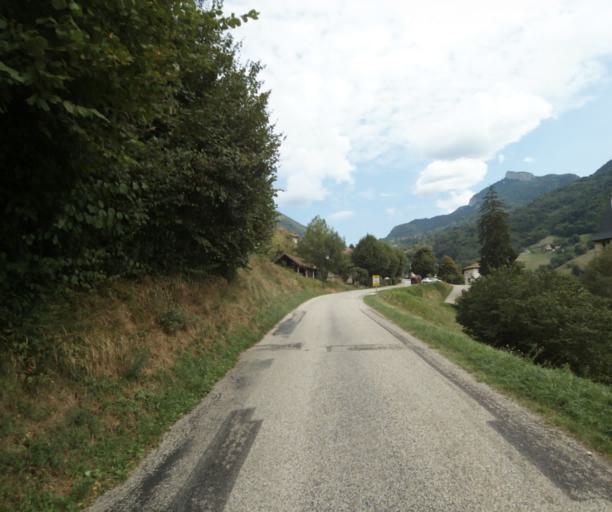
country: FR
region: Rhone-Alpes
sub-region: Departement de l'Isere
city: Saint-Egreve
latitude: 45.2617
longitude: 5.6985
